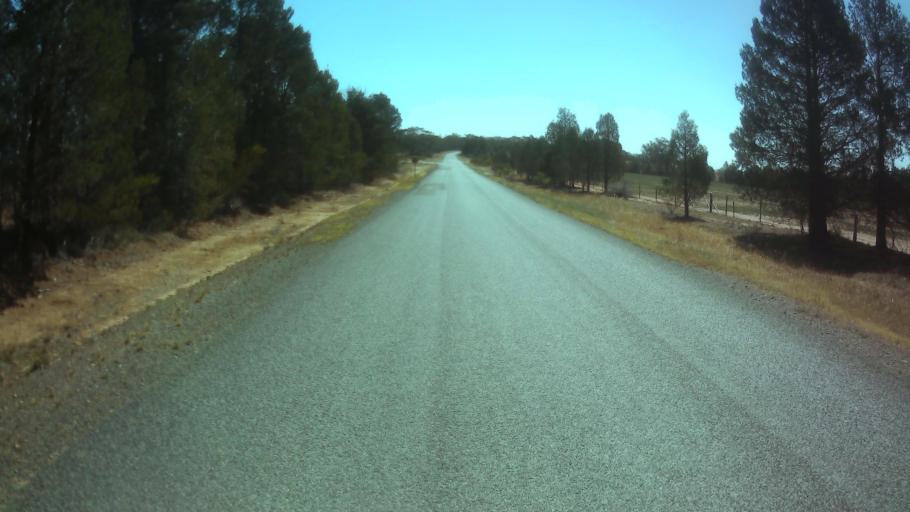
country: AU
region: New South Wales
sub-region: Weddin
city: Grenfell
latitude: -33.7549
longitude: 147.8328
